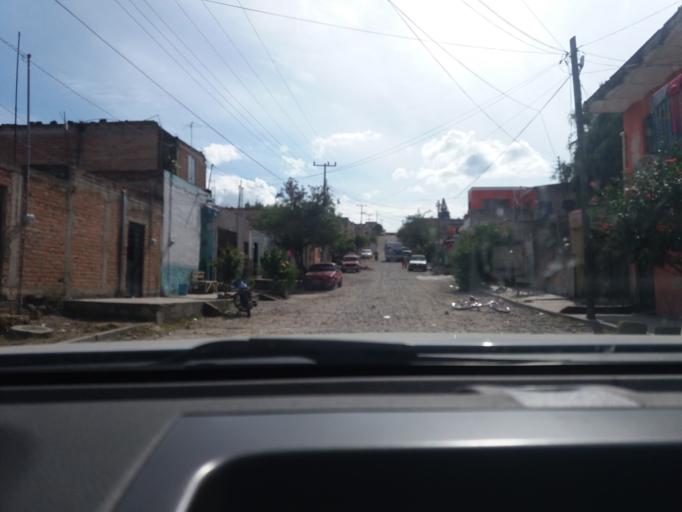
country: MX
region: Jalisco
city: Tala
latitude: 20.6593
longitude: -103.6942
